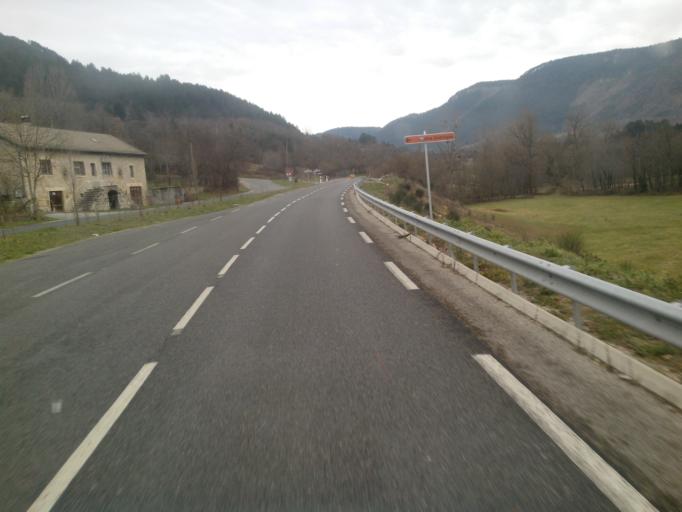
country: FR
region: Languedoc-Roussillon
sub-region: Departement de la Lozere
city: Mende
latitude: 44.4652
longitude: 3.5150
